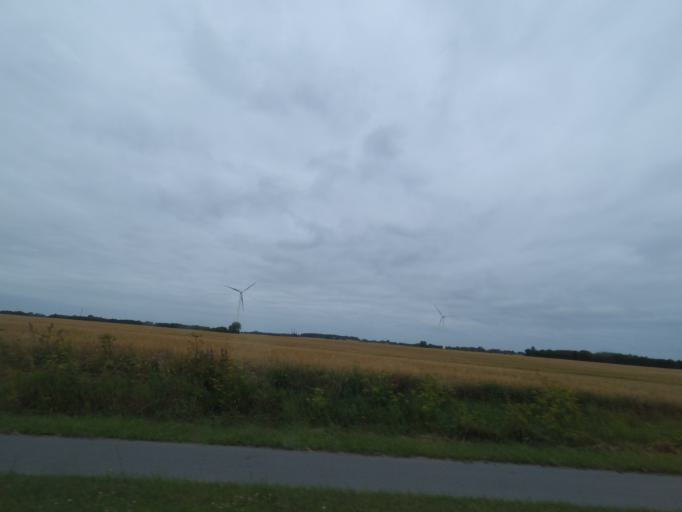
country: DK
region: South Denmark
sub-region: Nordfyns Kommune
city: Otterup
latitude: 55.5318
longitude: 10.4226
